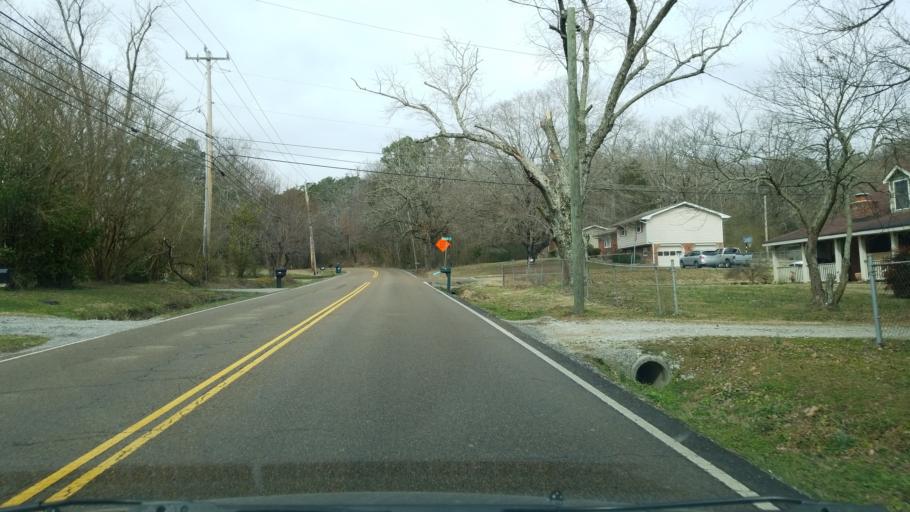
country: US
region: Tennessee
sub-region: Hamilton County
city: East Brainerd
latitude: 35.0008
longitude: -85.1097
